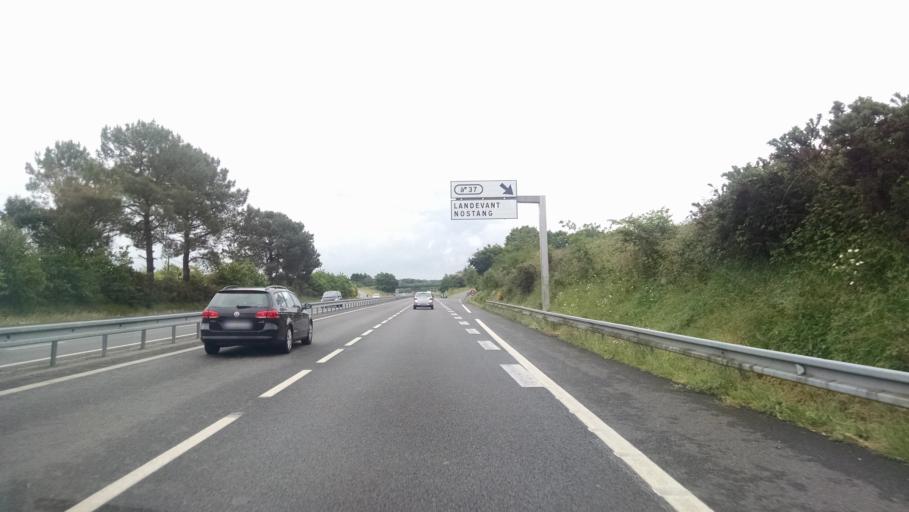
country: FR
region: Brittany
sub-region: Departement du Morbihan
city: Landevant
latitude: 47.7606
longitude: -3.1367
